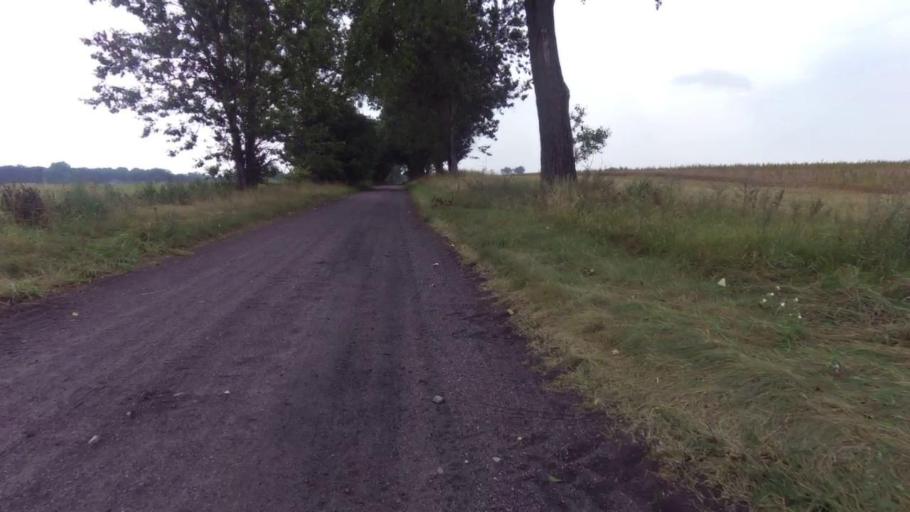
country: PL
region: West Pomeranian Voivodeship
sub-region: Powiat stargardzki
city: Suchan
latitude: 53.2351
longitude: 15.3832
